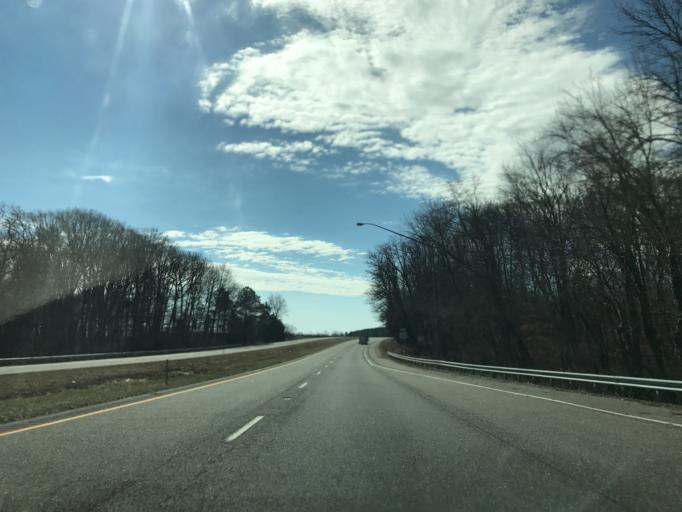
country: US
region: Delaware
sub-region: New Castle County
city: Townsend
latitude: 39.3611
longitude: -75.8176
